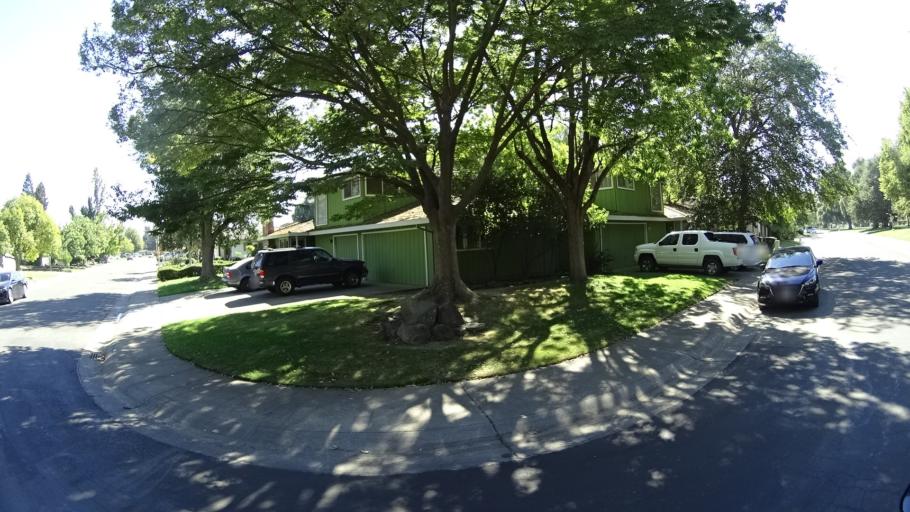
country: US
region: California
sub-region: Sacramento County
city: Parkway
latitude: 38.5013
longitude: -121.5265
